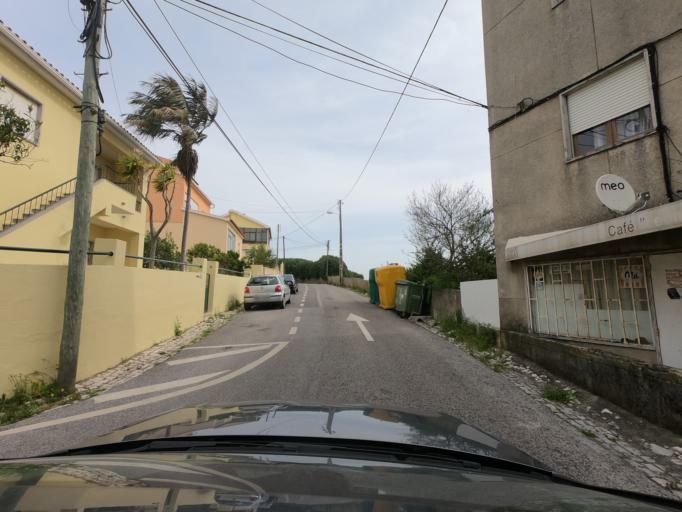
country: PT
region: Lisbon
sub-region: Oeiras
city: Porto Salvo
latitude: 38.7196
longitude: -9.2905
